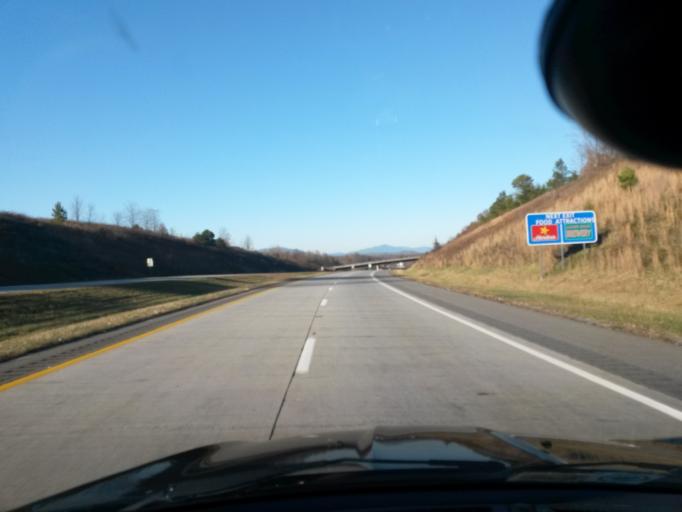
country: US
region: Virginia
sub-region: Amherst County
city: Amherst
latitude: 37.5471
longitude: -79.0681
